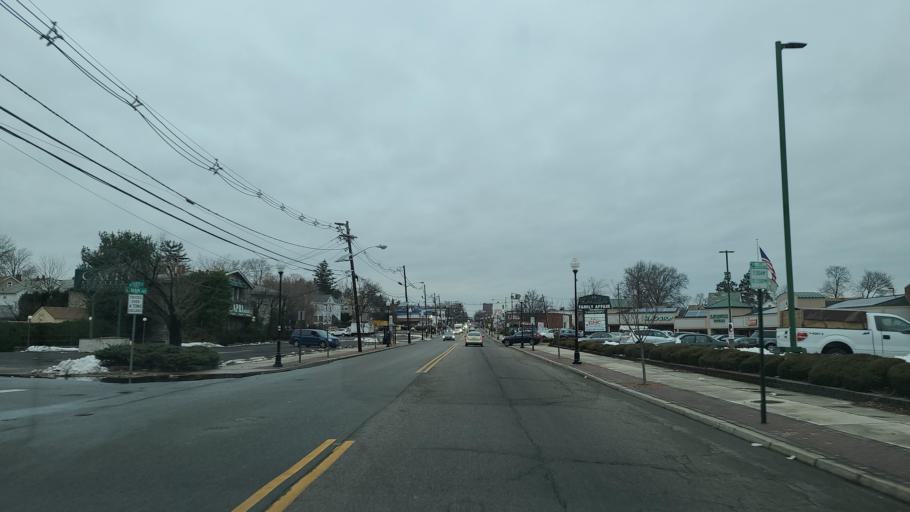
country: US
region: New Jersey
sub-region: Passaic County
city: Clifton
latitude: 40.8870
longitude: -74.1517
